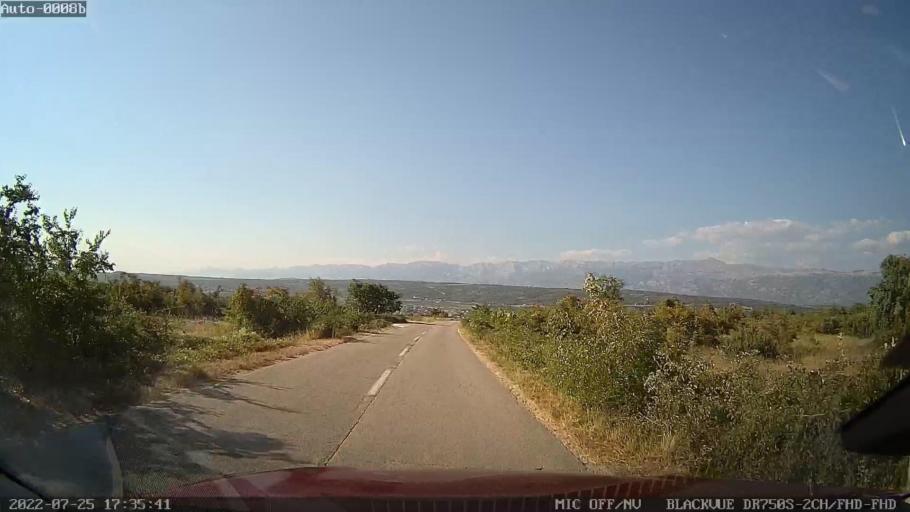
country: HR
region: Zadarska
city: Posedarje
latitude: 44.1929
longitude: 15.4725
